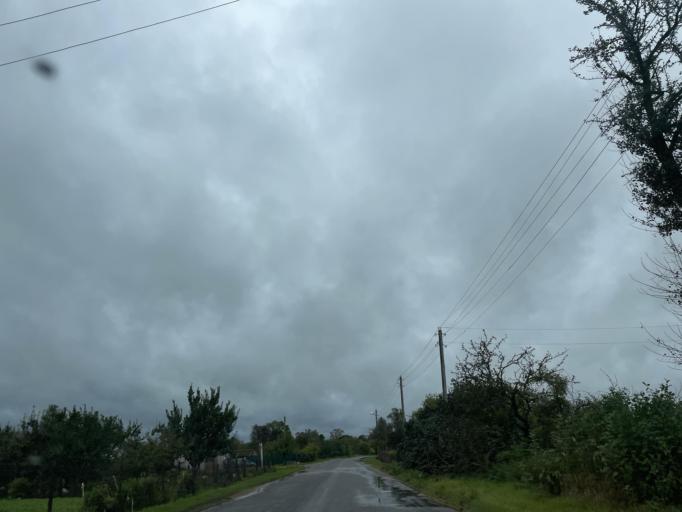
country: BY
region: Brest
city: Lyakhavichy
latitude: 53.1801
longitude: 26.2589
